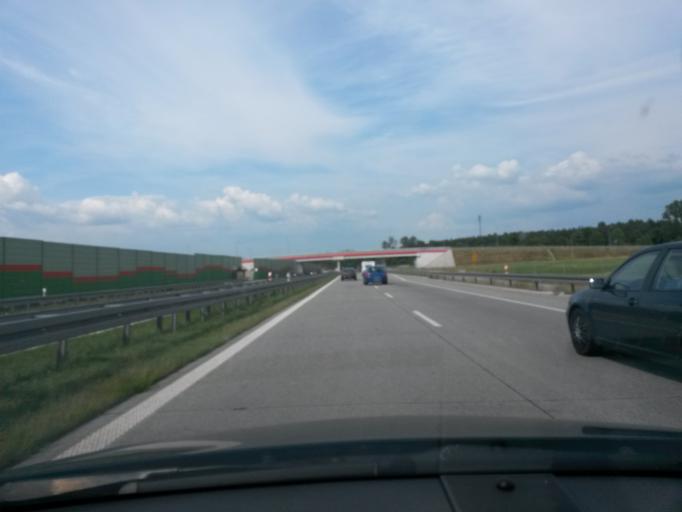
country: PL
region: Lodz Voivodeship
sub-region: Powiat tomaszowski
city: Czerniewice
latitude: 51.6925
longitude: 20.2108
